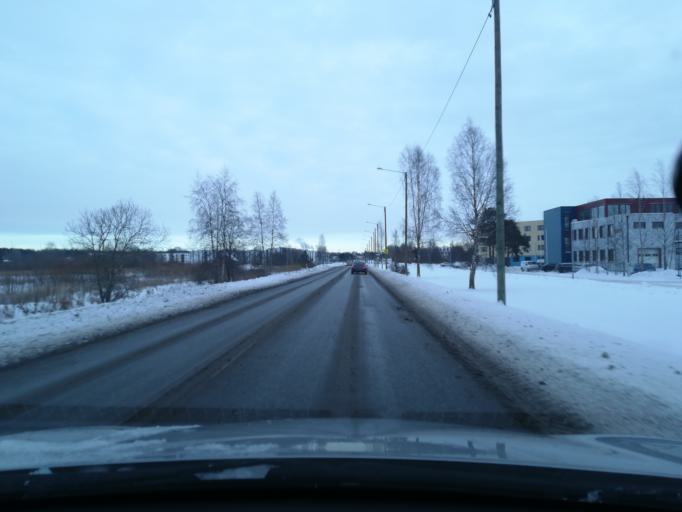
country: EE
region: Harju
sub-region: Harku vald
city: Tabasalu
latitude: 59.4304
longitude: 24.6090
